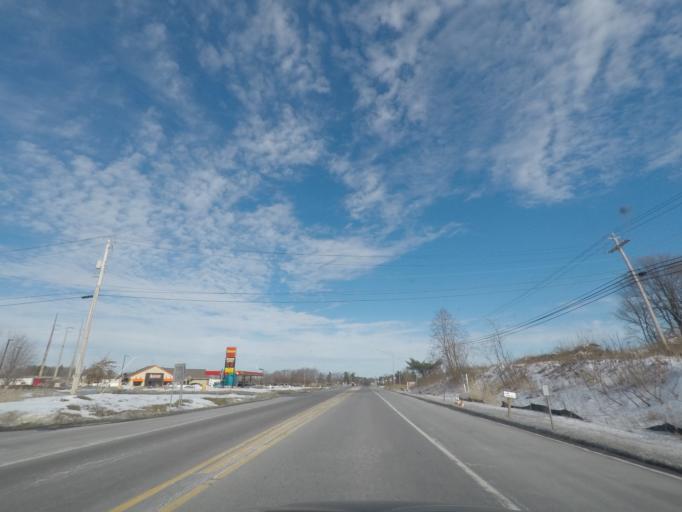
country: US
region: New York
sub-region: Schenectady County
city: Rotterdam
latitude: 42.7804
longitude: -74.0298
